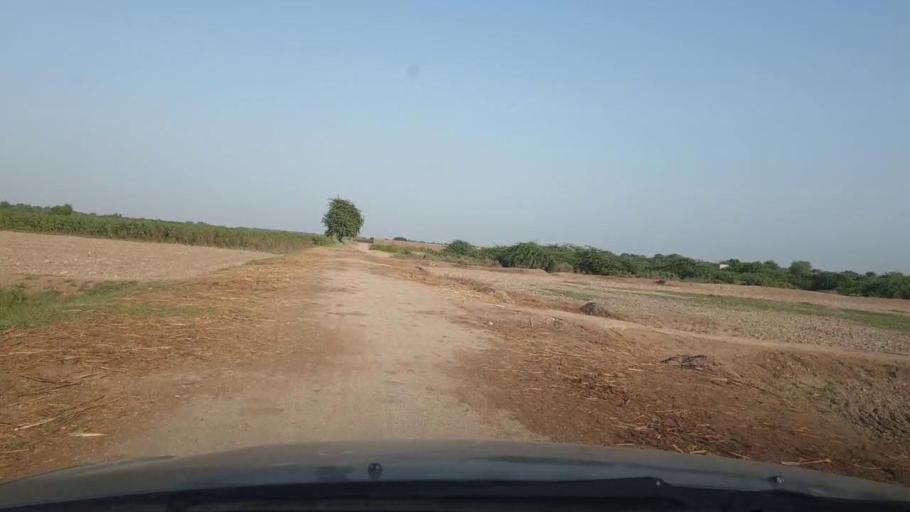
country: PK
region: Sindh
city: Tando Ghulam Ali
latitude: 25.1717
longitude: 68.9536
